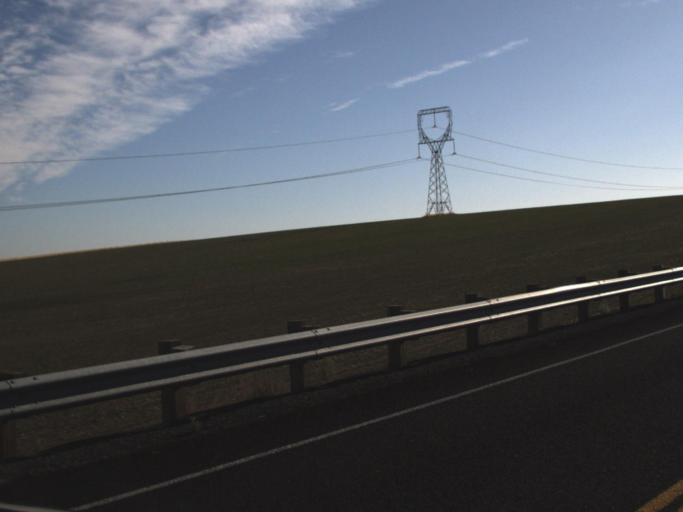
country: US
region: Washington
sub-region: Franklin County
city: Connell
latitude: 46.6221
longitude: -118.7155
